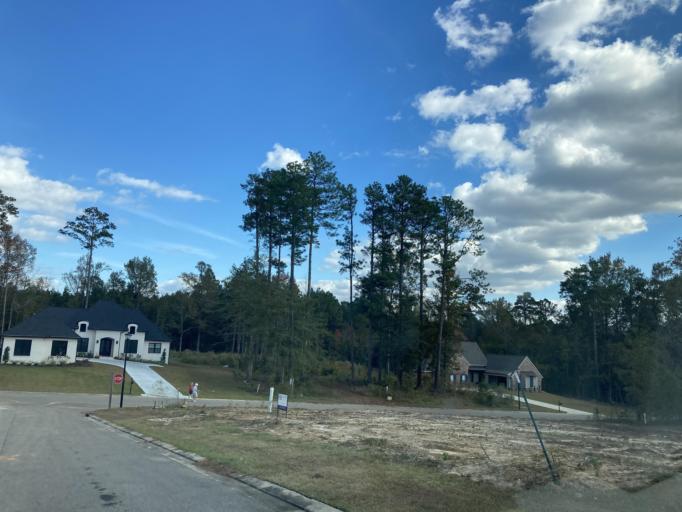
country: US
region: Mississippi
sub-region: Lamar County
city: Arnold Line
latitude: 31.3450
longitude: -89.3666
